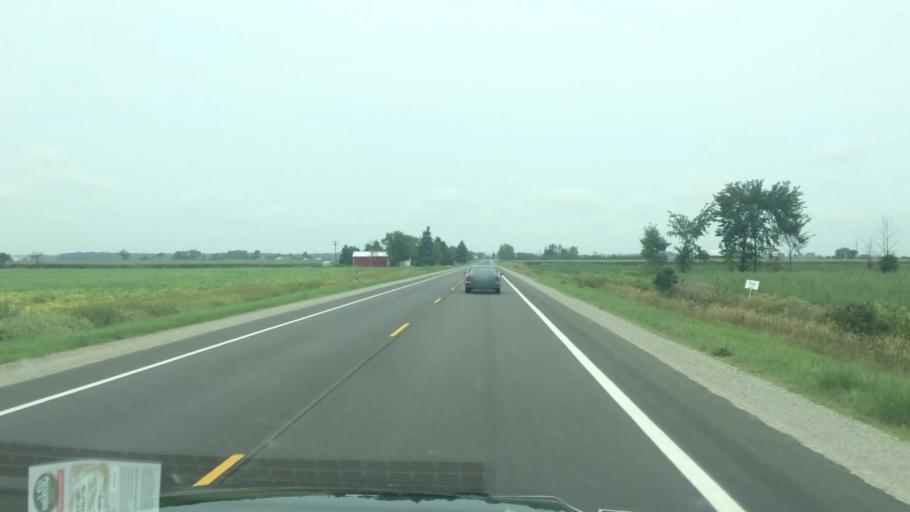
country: US
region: Michigan
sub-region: Huron County
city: Bad Axe
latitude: 43.9902
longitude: -83.0073
